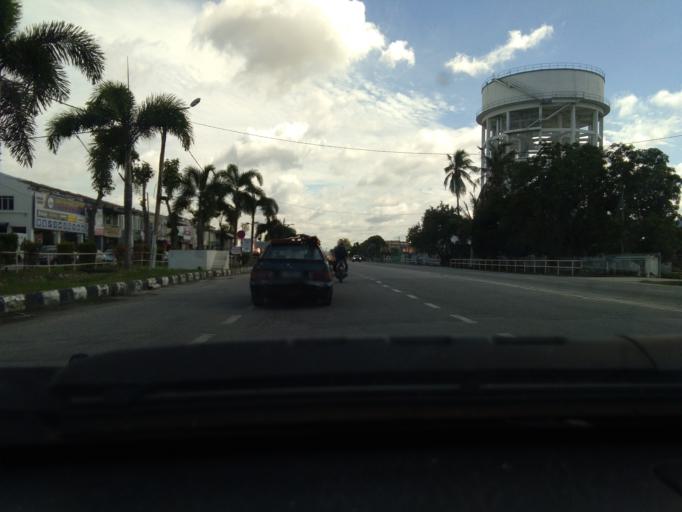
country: MY
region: Perak
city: Parit Buntar
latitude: 5.1116
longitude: 100.4823
